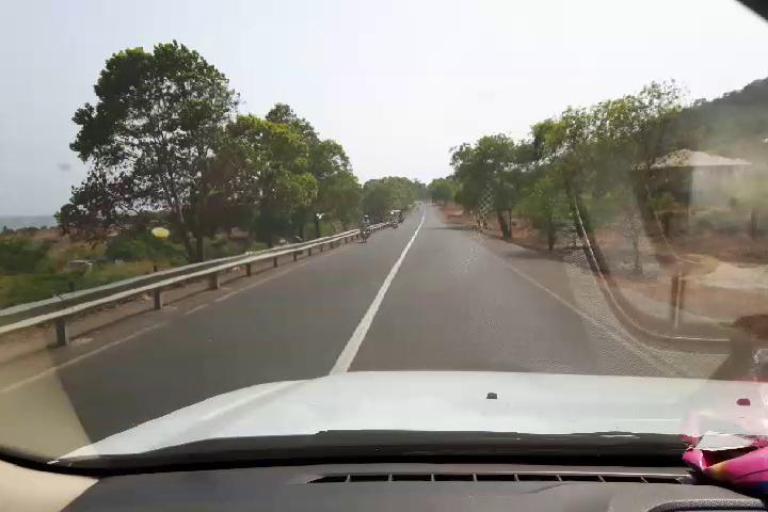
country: SL
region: Western Area
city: Waterloo
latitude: 8.2039
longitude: -13.1114
